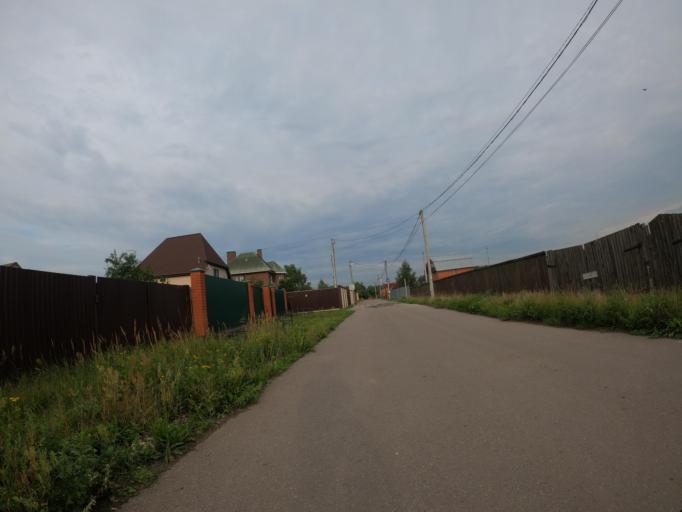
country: RU
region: Moskovskaya
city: Bykovo
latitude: 55.6548
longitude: 38.1073
